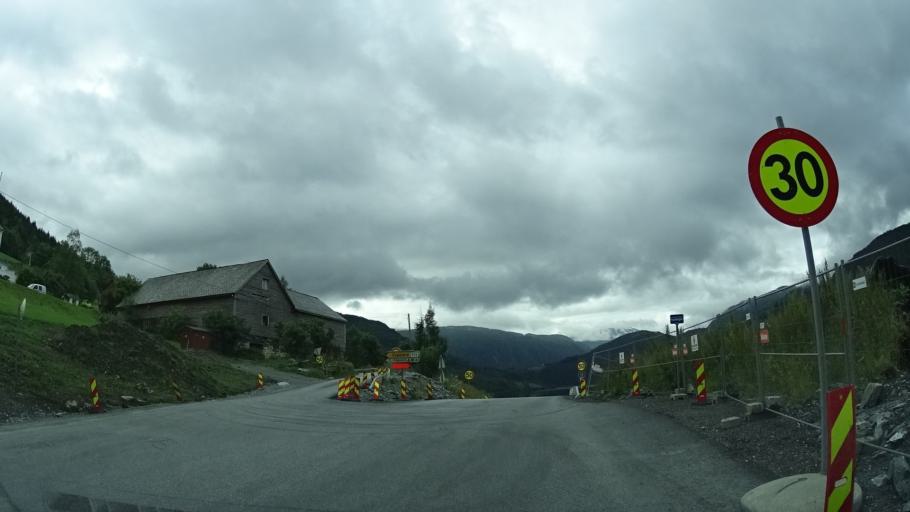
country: NO
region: Hordaland
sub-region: Granvin
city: Granvin
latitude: 60.5659
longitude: 6.7245
